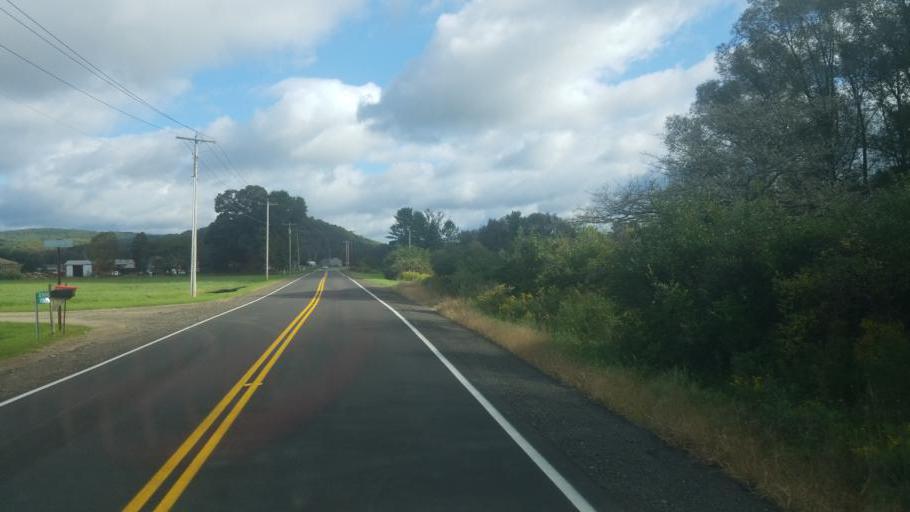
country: US
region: New York
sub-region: Cattaraugus County
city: Weston Mills
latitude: 42.0843
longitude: -78.3677
